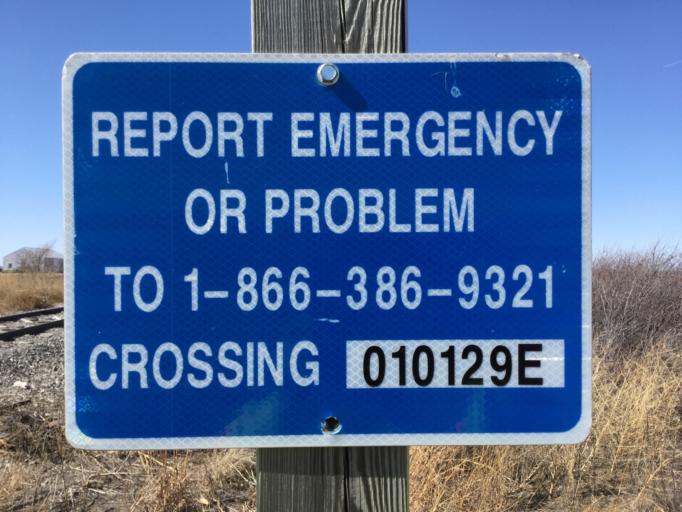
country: US
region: Kansas
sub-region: Pawnee County
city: Larned
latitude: 38.1664
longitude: -99.2142
